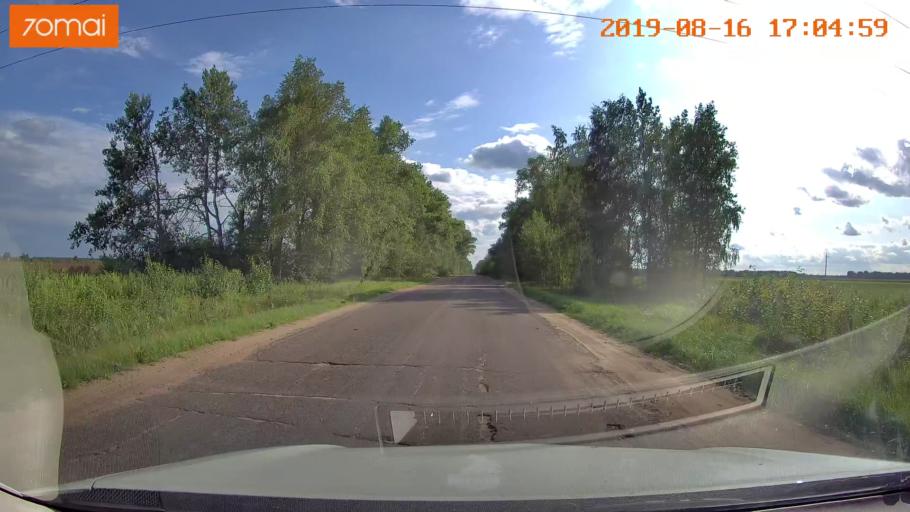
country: BY
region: Mogilev
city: Yalizava
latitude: 53.2406
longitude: 28.9475
